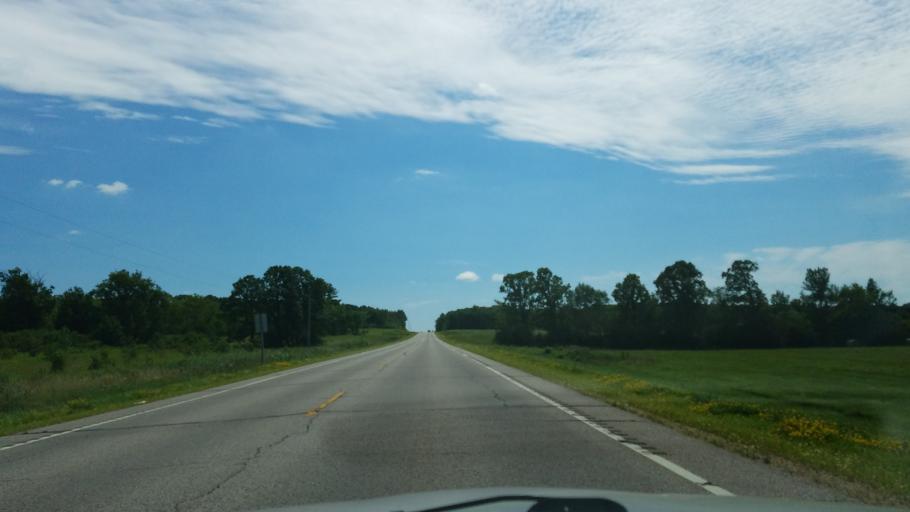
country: US
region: Wisconsin
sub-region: Saint Croix County
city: Glenwood City
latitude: 44.9859
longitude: -92.1965
